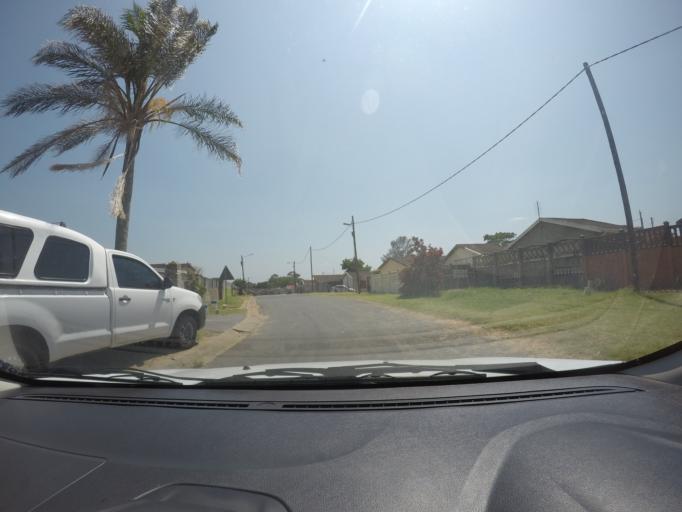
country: ZA
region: KwaZulu-Natal
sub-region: uThungulu District Municipality
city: eSikhawini
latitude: -28.8688
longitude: 31.9252
